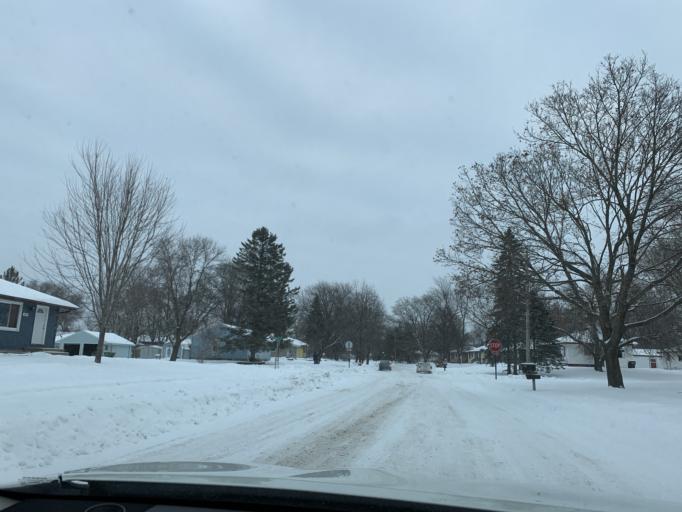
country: US
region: Minnesota
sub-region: Anoka County
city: Blaine
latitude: 45.1748
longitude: -93.2839
